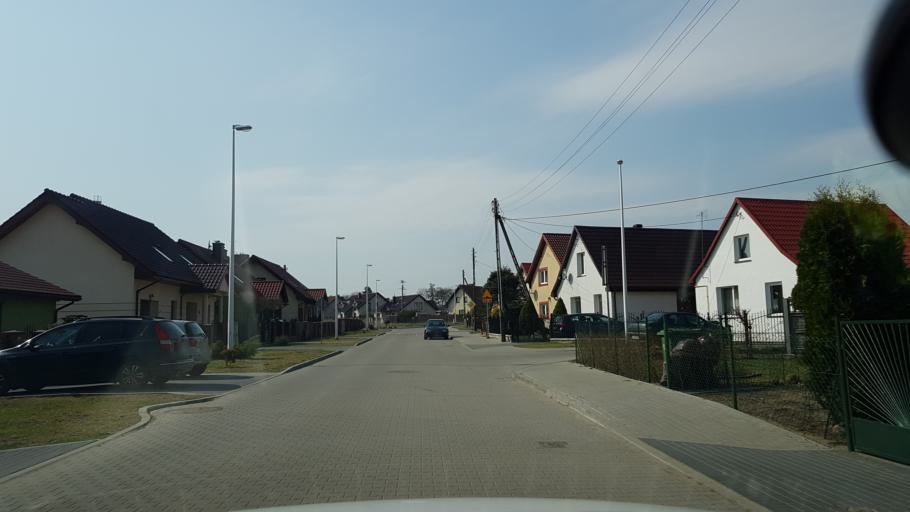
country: PL
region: West Pomeranian Voivodeship
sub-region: Powiat stargardzki
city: Stargard Szczecinski
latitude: 53.3449
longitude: 15.0696
